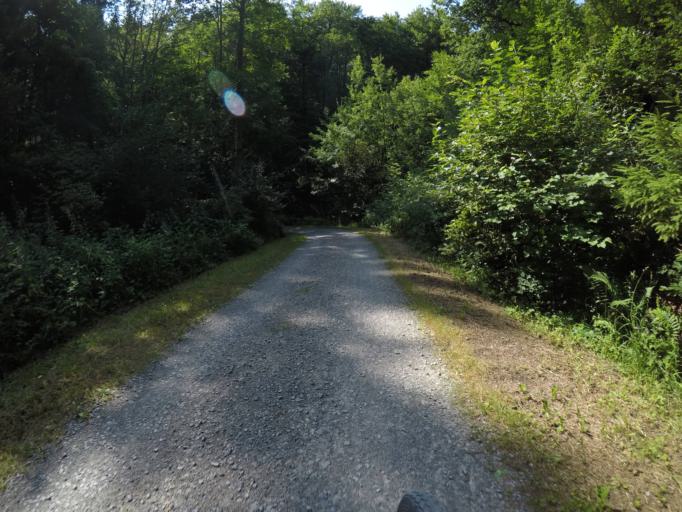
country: DE
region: Baden-Wuerttemberg
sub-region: Regierungsbezirk Stuttgart
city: Schlaitdorf
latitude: 48.6251
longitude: 9.1954
